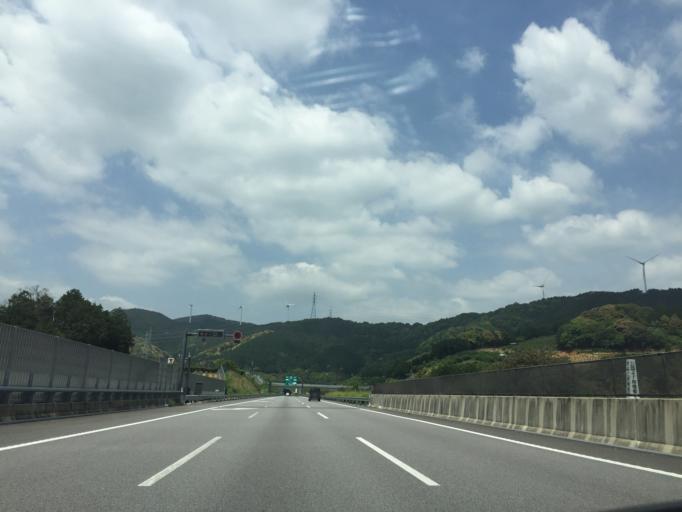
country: JP
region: Shizuoka
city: Hamakita
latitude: 34.8495
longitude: 137.7221
